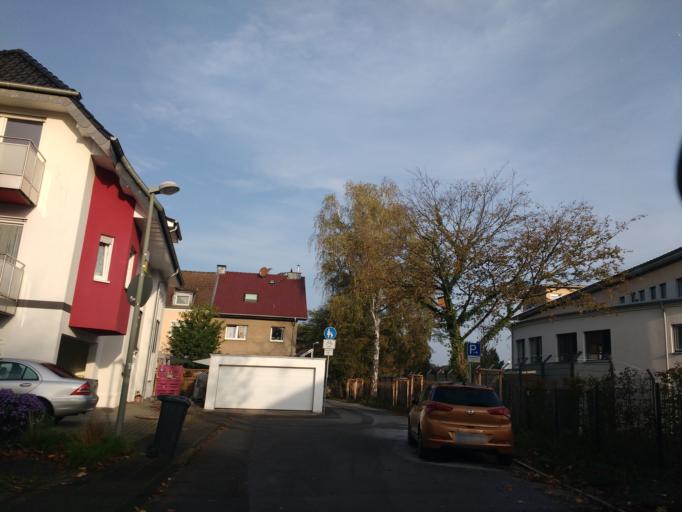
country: DE
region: North Rhine-Westphalia
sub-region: Regierungsbezirk Detmold
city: Paderborn
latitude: 51.7176
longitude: 8.7643
